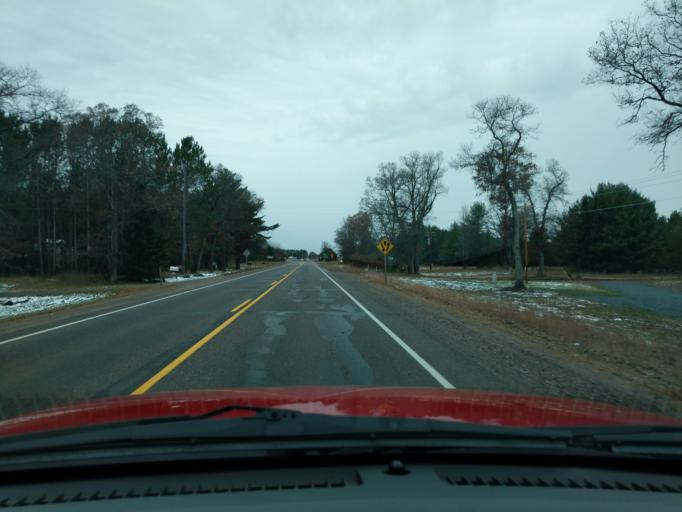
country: US
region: Wisconsin
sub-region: Burnett County
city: Siren
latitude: 45.8167
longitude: -92.3559
